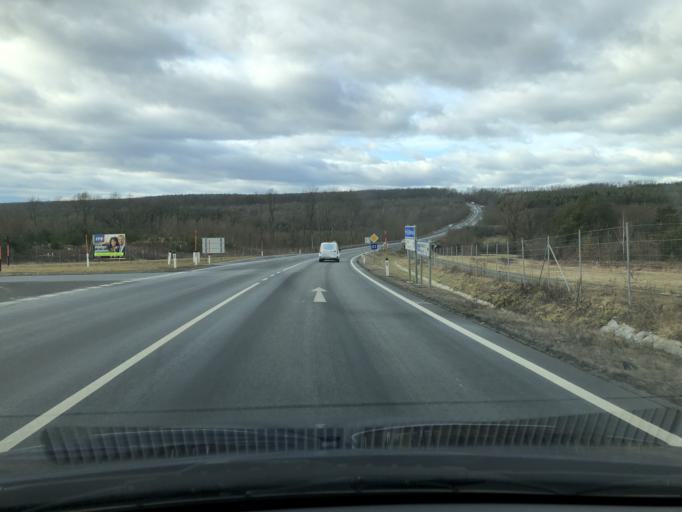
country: AT
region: Burgenland
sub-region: Politischer Bezirk Oberwart
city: Hannersdorf
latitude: 47.2612
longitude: 16.3734
